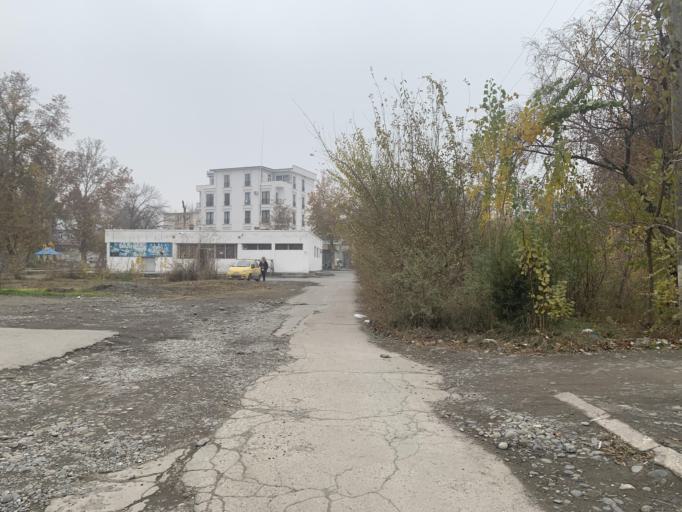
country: UZ
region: Fergana
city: Qo`qon
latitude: 40.5431
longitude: 70.9228
